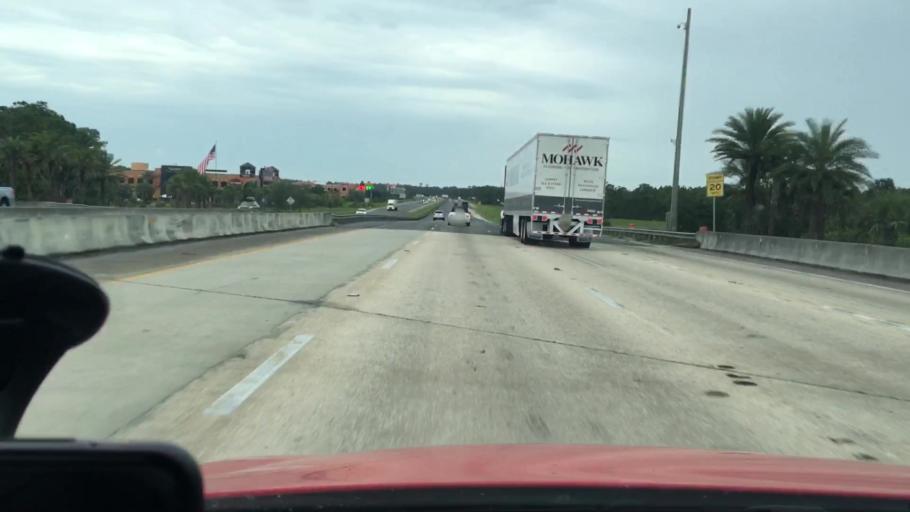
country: US
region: Florida
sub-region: Volusia County
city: Ormond-by-the-Sea
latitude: 29.3350
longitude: -81.1321
